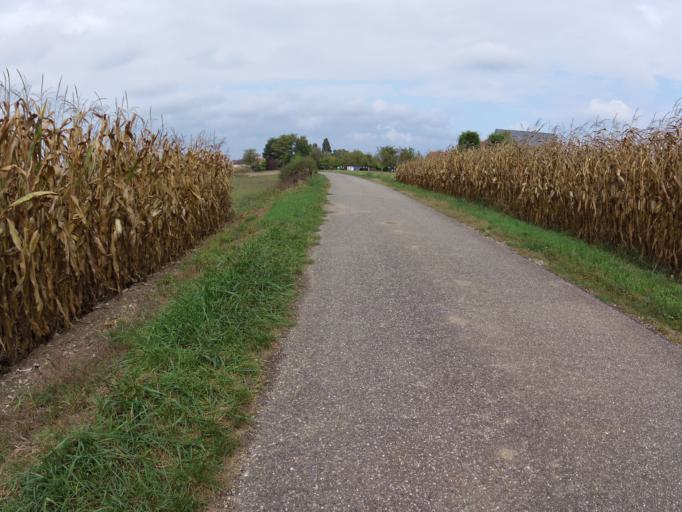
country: FR
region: Alsace
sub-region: Departement du Haut-Rhin
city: Biesheim
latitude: 48.0358
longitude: 7.5398
